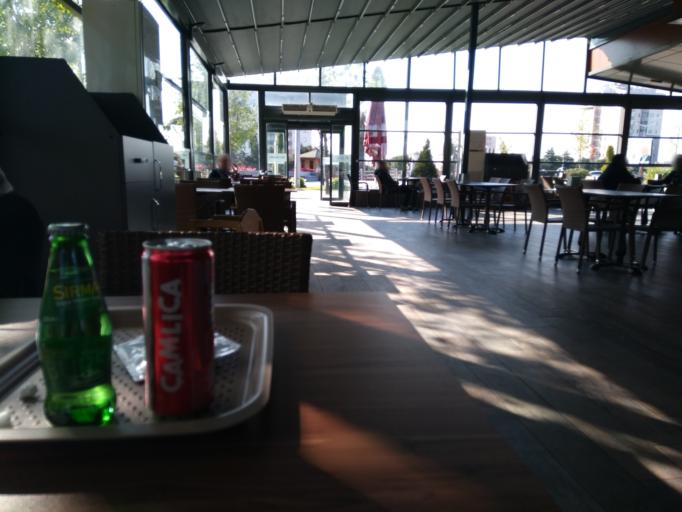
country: TR
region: Istanbul
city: Mahmutbey
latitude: 41.0452
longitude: 28.7935
